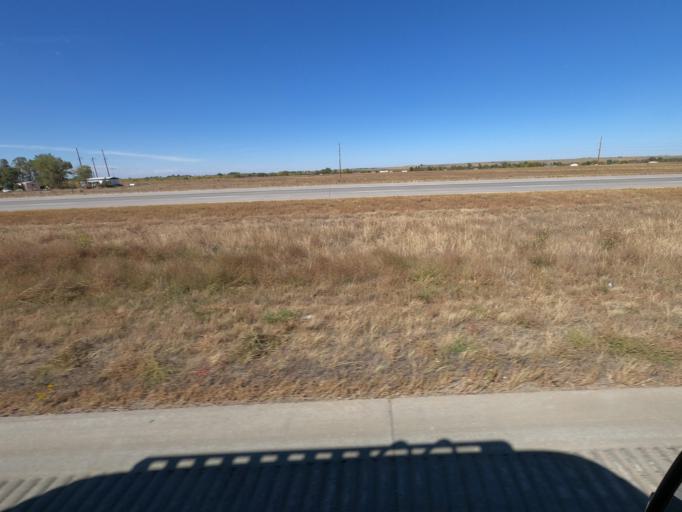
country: US
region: Colorado
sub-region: Morgan County
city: Fort Morgan
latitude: 40.2642
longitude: -103.8648
